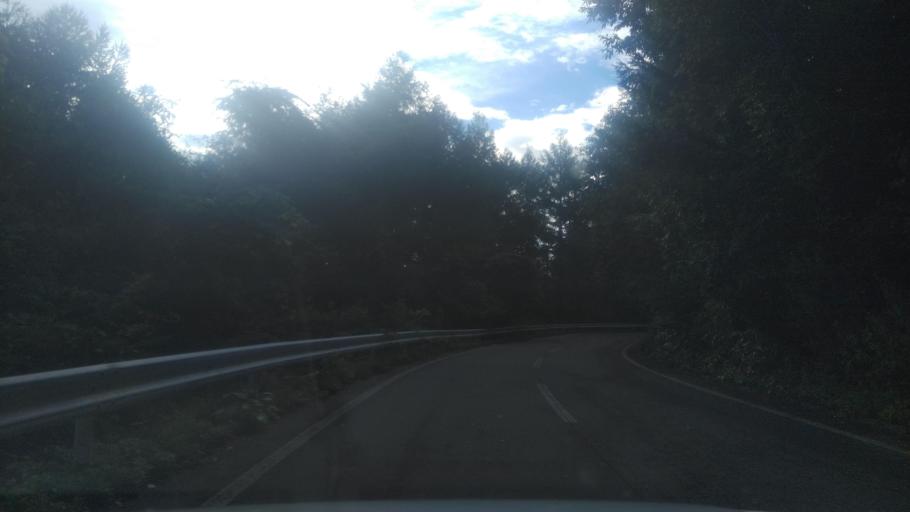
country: JP
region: Nagano
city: Ueda
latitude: 36.5093
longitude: 138.3684
